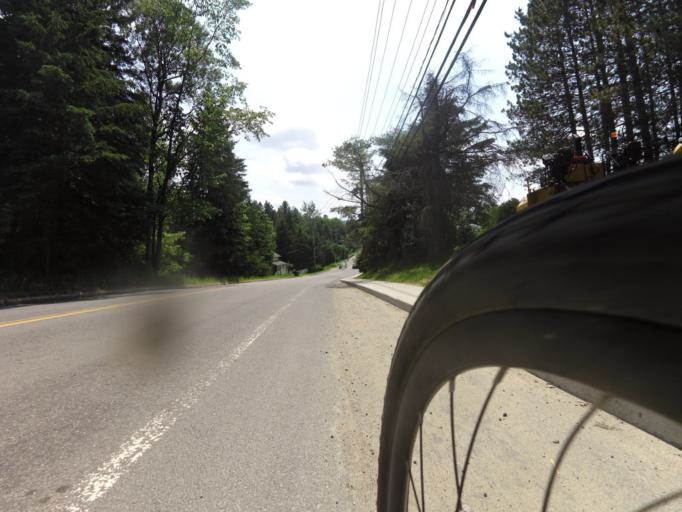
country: CA
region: Quebec
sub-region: Laurentides
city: Mont-Tremblant
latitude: 46.1274
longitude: -74.5913
